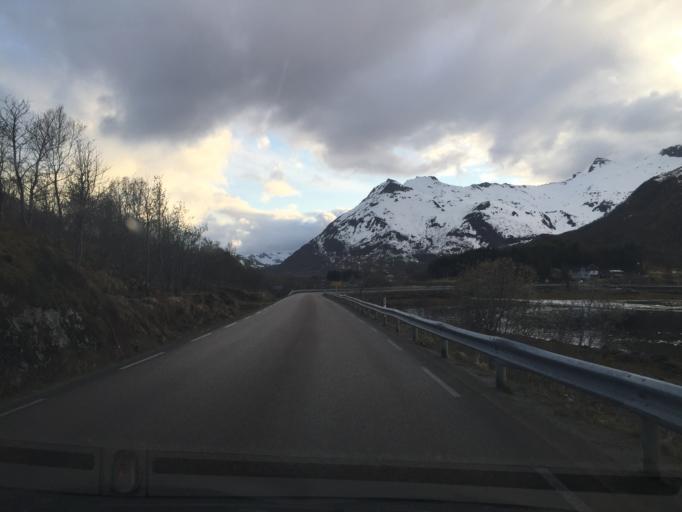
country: NO
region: Nordland
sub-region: Vagan
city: Svolvaer
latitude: 68.3244
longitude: 14.6952
